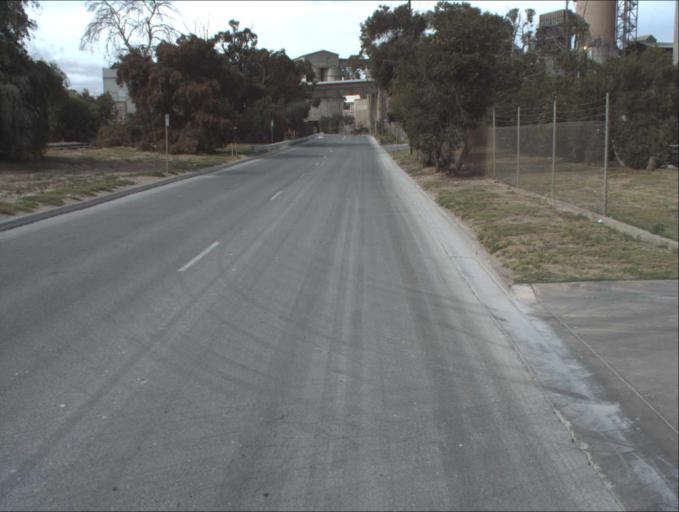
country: AU
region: South Australia
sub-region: Port Adelaide Enfield
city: Birkenhead
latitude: -34.8296
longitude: 138.5041
